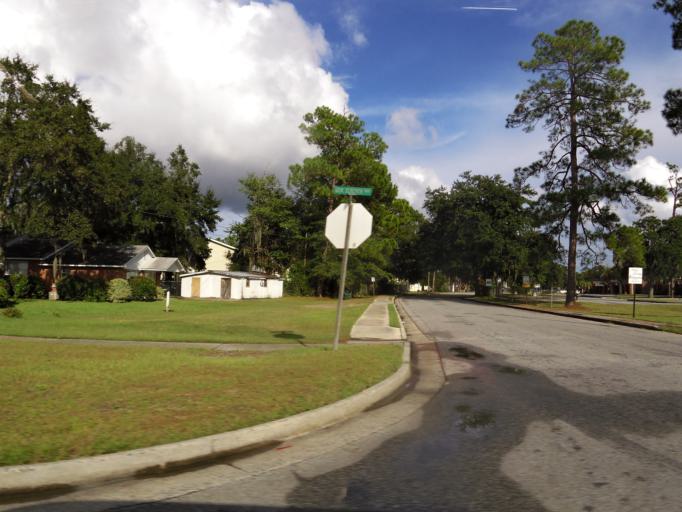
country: US
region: Georgia
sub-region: Liberty County
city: Hinesville
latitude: 31.8504
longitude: -81.6059
